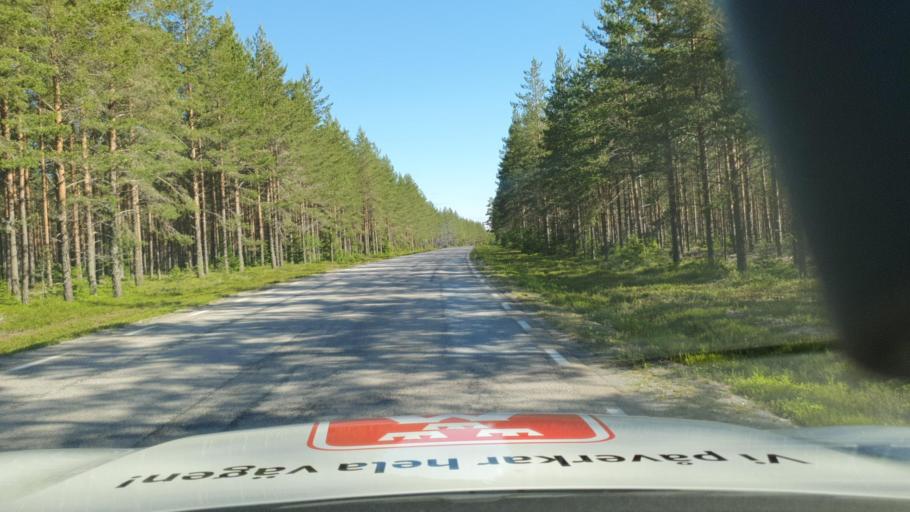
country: SE
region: Vaesterbotten
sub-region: Umea Kommun
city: Roback
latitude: 63.8640
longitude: 20.1446
